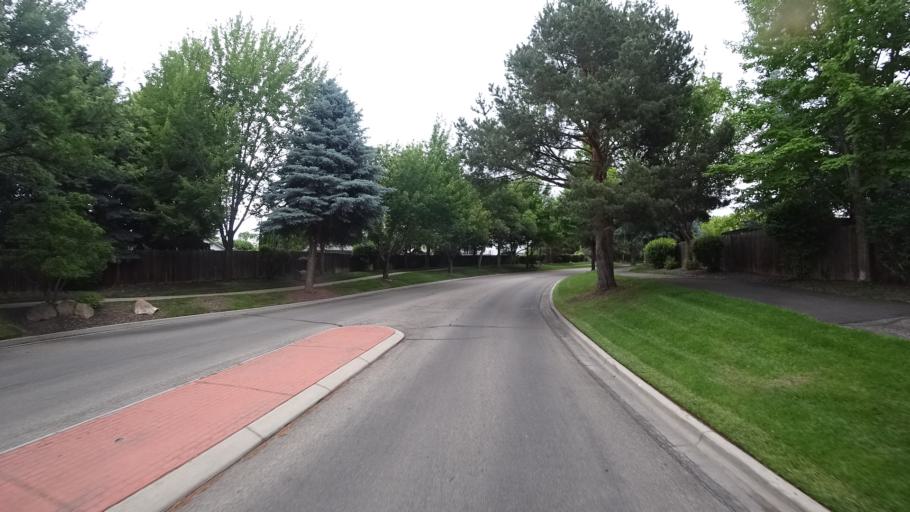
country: US
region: Idaho
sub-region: Ada County
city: Meridian
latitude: 43.5867
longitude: -116.3321
